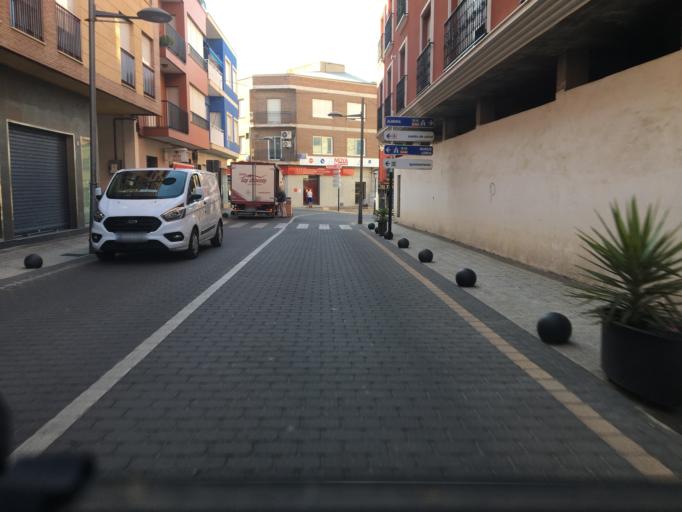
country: ES
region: Murcia
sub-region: Murcia
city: Puerto Lumbreras
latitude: 37.5618
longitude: -1.8098
